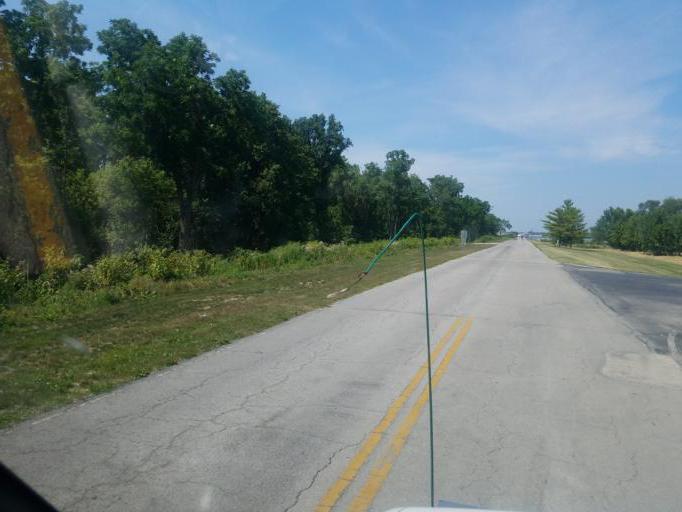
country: US
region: Ohio
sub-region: Mercer County
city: Celina
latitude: 40.5262
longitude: -84.5747
